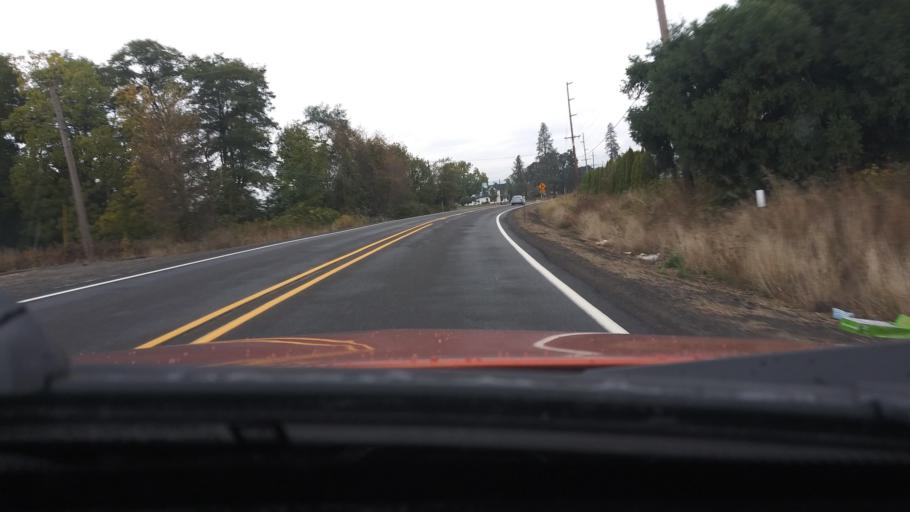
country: US
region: Oregon
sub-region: Washington County
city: Banks
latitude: 45.5825
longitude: -123.1141
